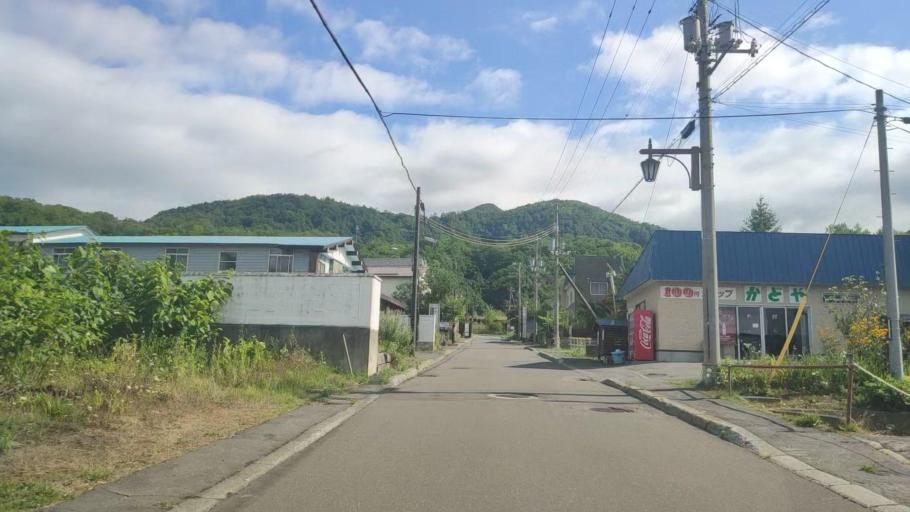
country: JP
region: Hokkaido
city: Date
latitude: 42.5630
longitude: 140.8253
